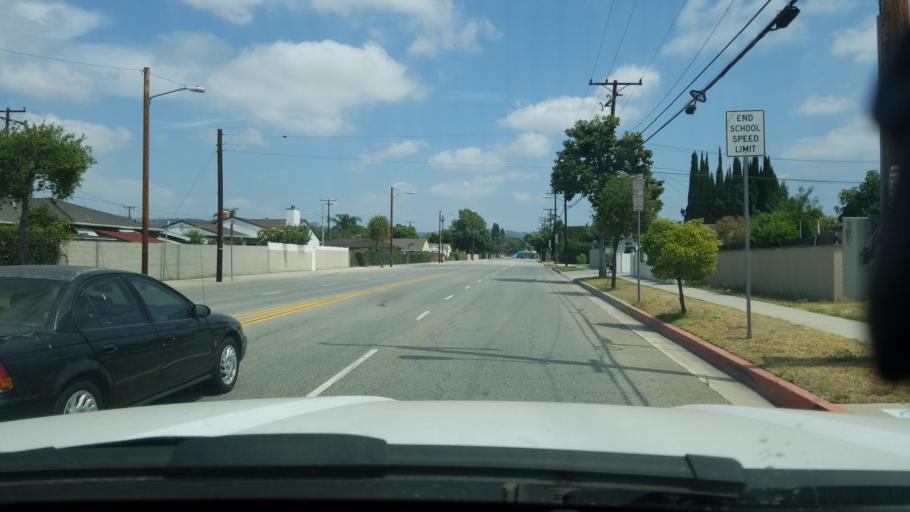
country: US
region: California
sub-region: Los Angeles County
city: South Whittier
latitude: 33.9403
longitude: -118.0331
